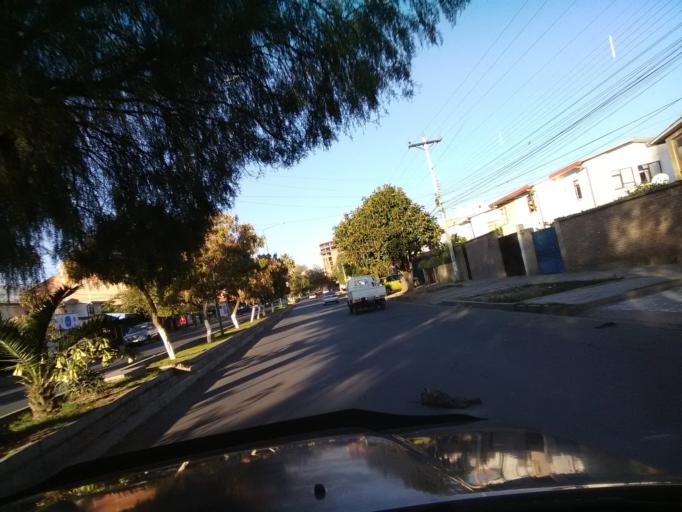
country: BO
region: Cochabamba
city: Cochabamba
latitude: -17.3710
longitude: -66.1867
